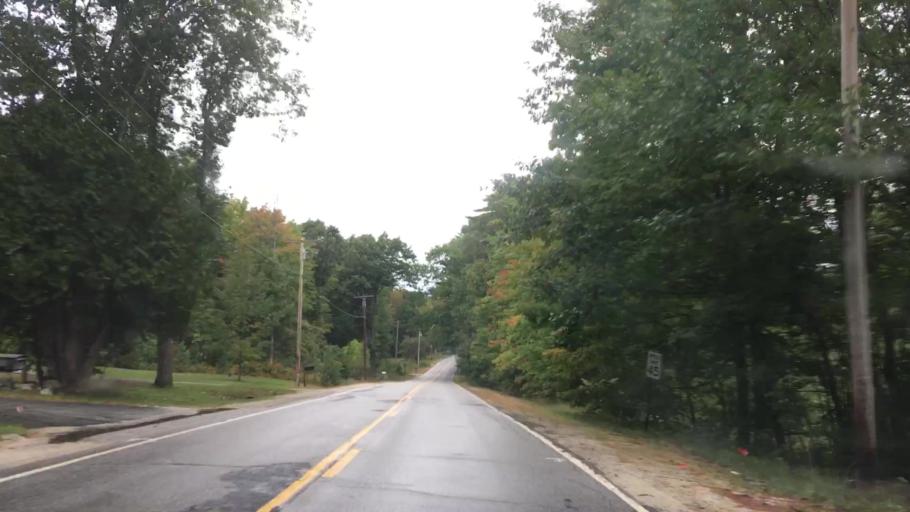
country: US
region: Maine
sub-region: Cumberland County
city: Raymond
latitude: 43.9642
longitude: -70.4653
